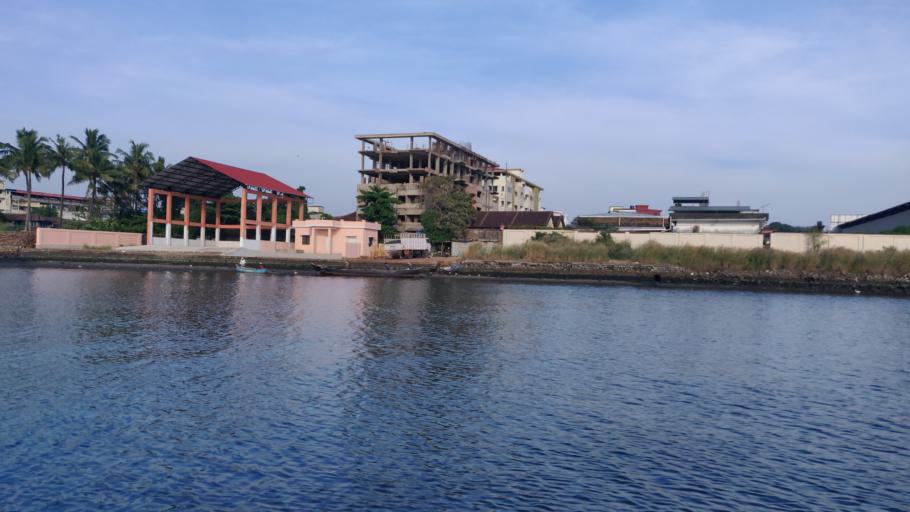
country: IN
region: Karnataka
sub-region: Dakshina Kannada
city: Mangalore
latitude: 12.8663
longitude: 74.8303
